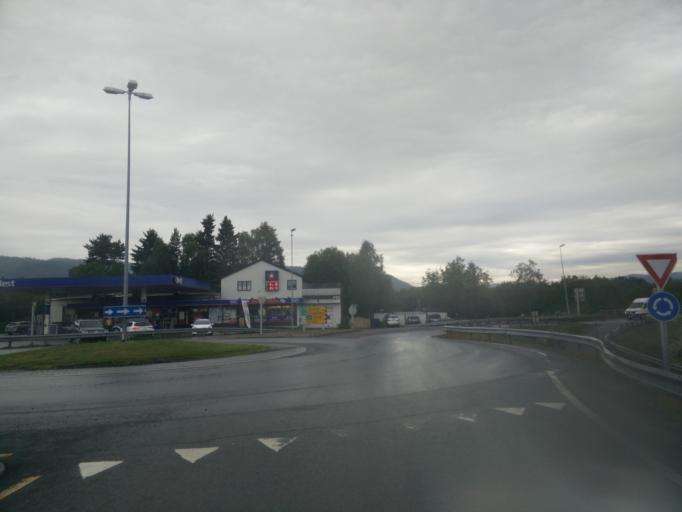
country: NO
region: Sor-Trondelag
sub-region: Orkdal
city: Orkanger
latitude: 63.2665
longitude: 9.8038
